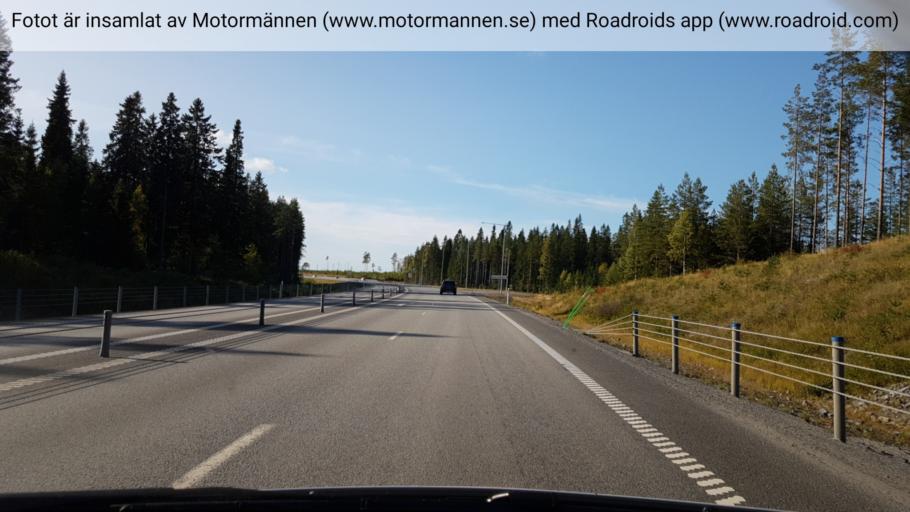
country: SE
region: Vaesterbotten
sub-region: Umea Kommun
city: Umea
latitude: 63.8525
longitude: 20.2878
